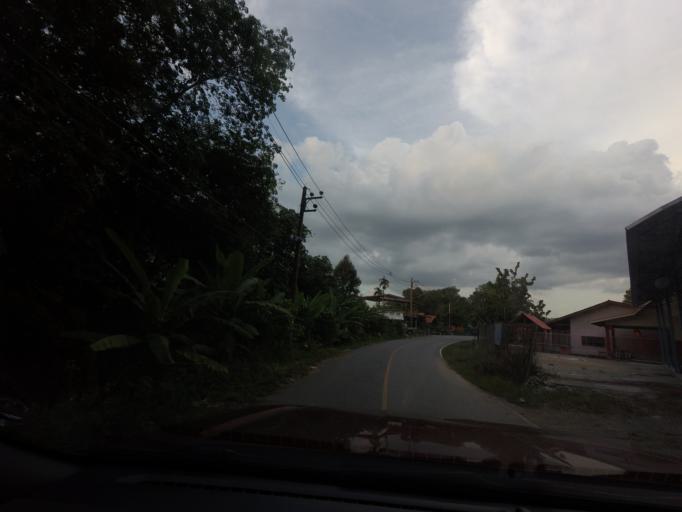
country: TH
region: Yala
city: Than To
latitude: 6.0108
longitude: 101.2289
